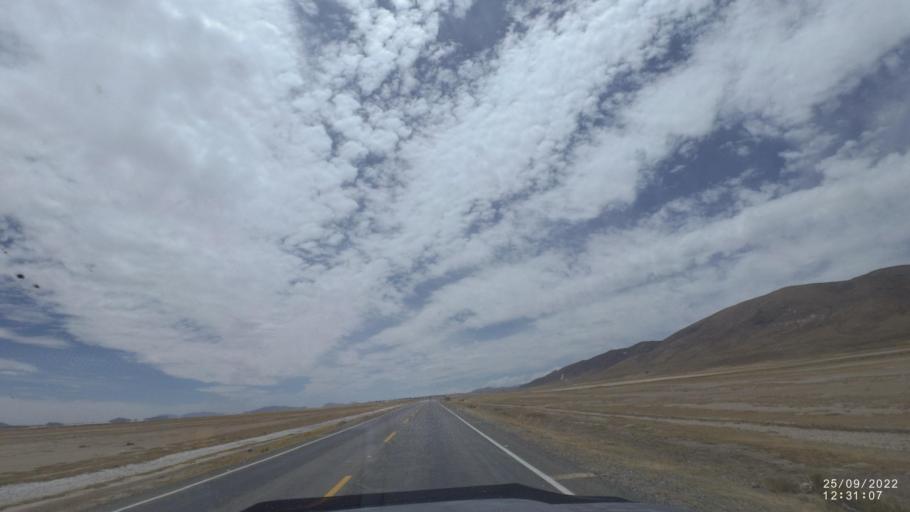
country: BO
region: Oruro
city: Machacamarca
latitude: -18.2380
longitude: -67.0042
